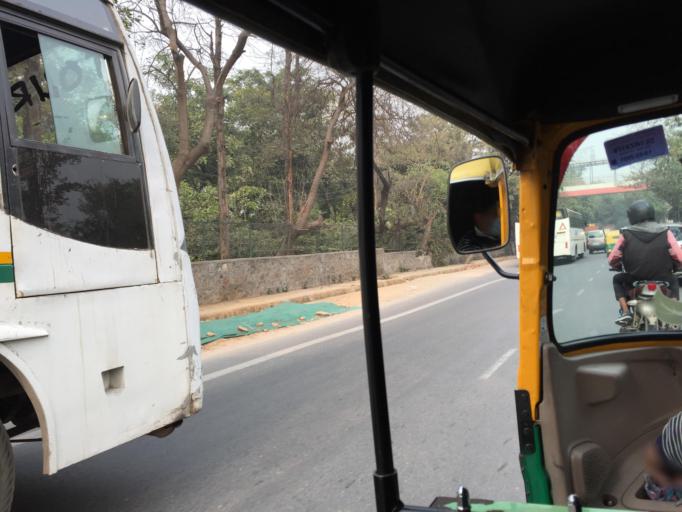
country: IN
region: NCT
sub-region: New Delhi
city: New Delhi
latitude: 28.5132
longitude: 77.1855
